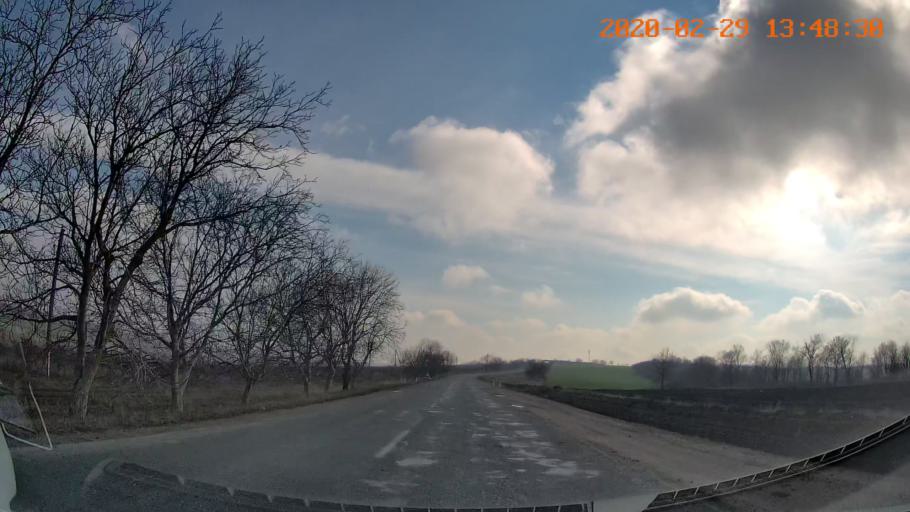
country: MD
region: Floresti
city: Leninskiy
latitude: 47.8536
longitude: 28.4862
